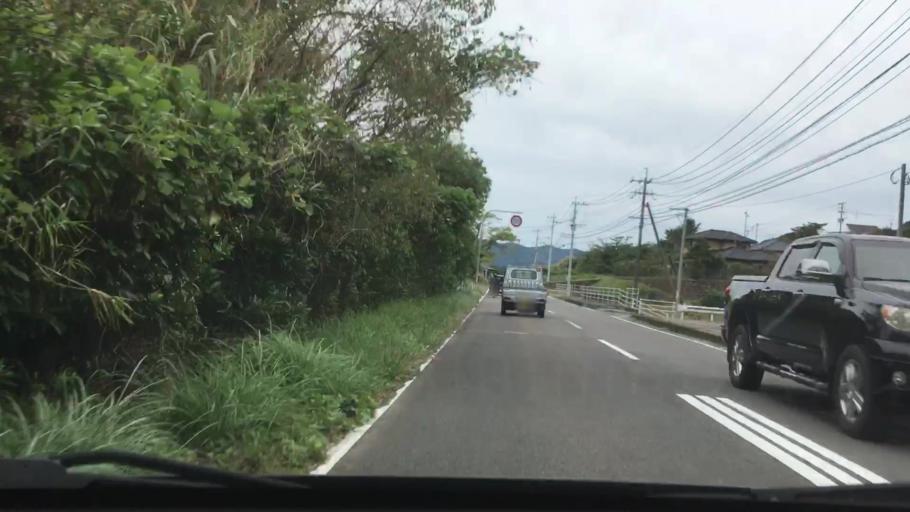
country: JP
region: Nagasaki
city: Sasebo
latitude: 33.0273
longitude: 129.7403
